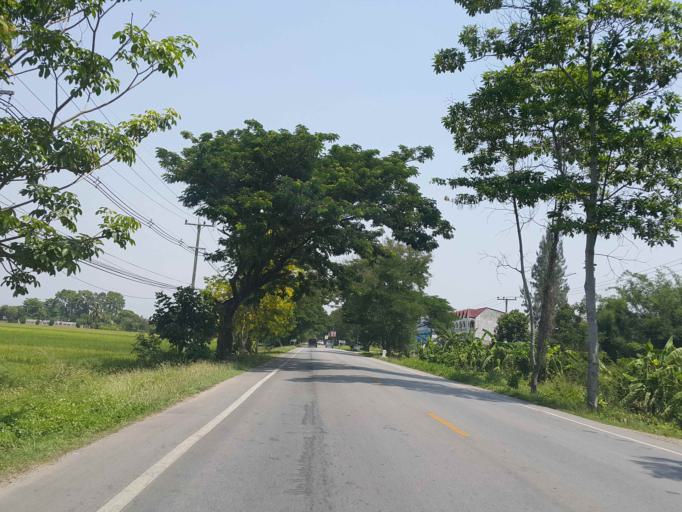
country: TH
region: Chiang Mai
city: Mae Taeng
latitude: 19.0242
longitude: 98.9686
